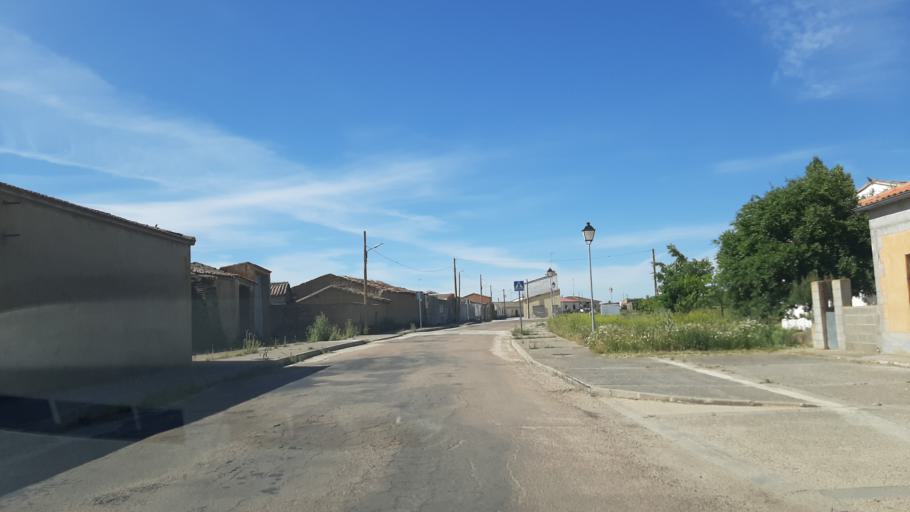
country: ES
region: Castille and Leon
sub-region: Provincia de Salamanca
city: Aldeaseca de Alba
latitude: 40.8195
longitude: -5.4480
